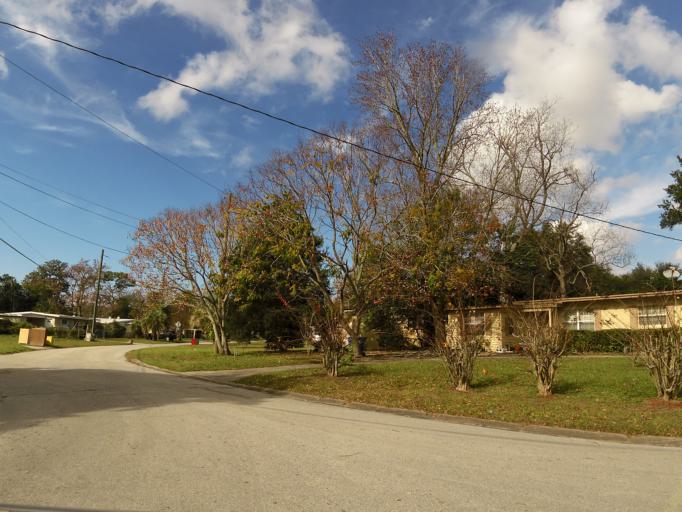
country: US
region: Florida
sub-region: Duval County
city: Jacksonville
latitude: 30.3402
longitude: -81.5844
